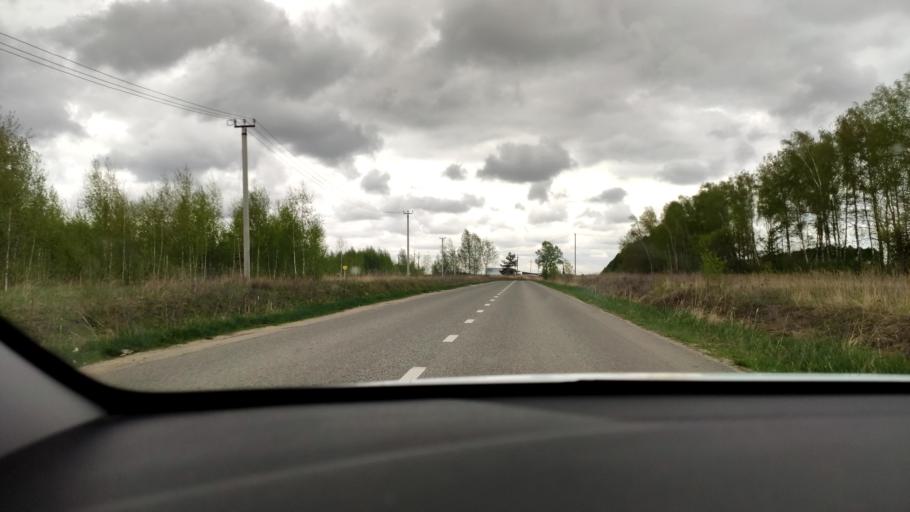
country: RU
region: Tatarstan
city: Vysokaya Gora
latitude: 55.8016
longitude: 49.3193
